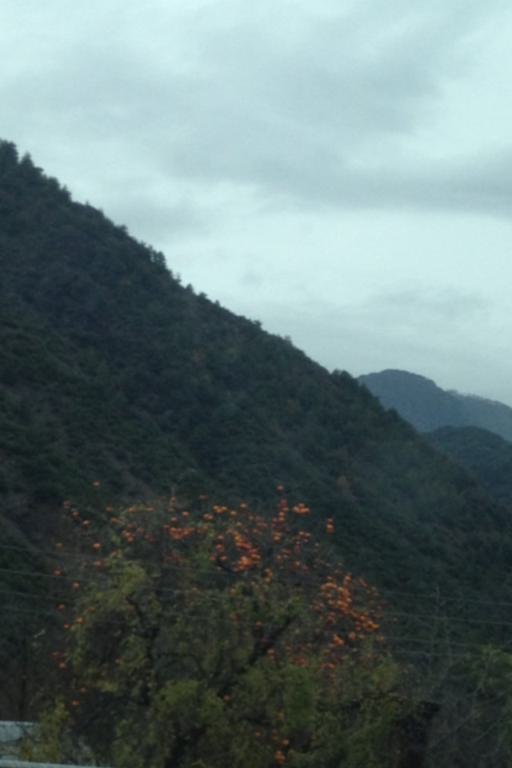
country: AL
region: Kukes
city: Kukes
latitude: 42.0716
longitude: 20.4606
